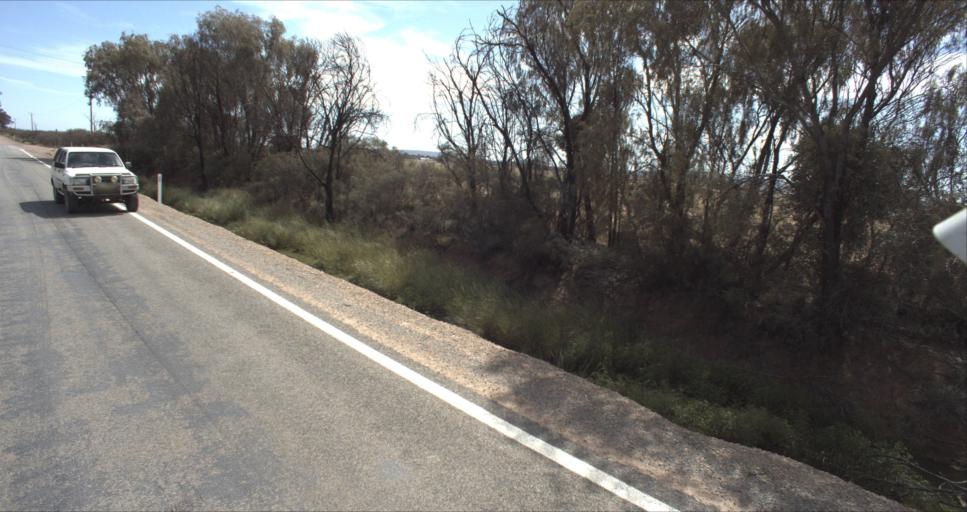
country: AU
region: New South Wales
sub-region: Leeton
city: Leeton
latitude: -34.5544
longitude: 146.4388
